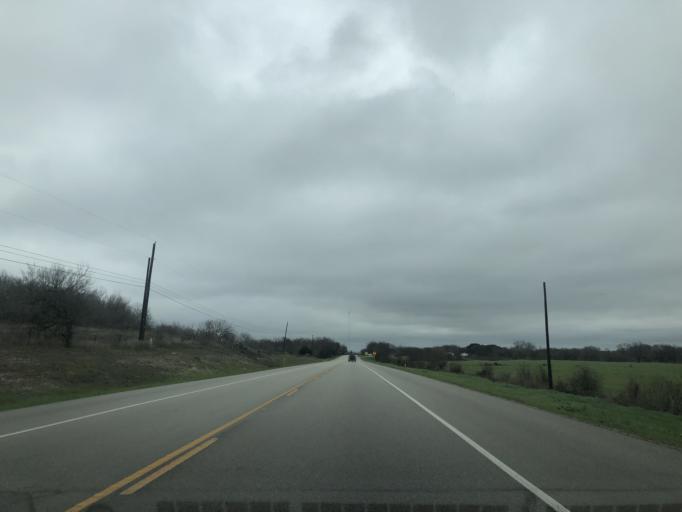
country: US
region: Texas
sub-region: Williamson County
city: Hutto
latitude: 30.6401
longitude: -97.5531
